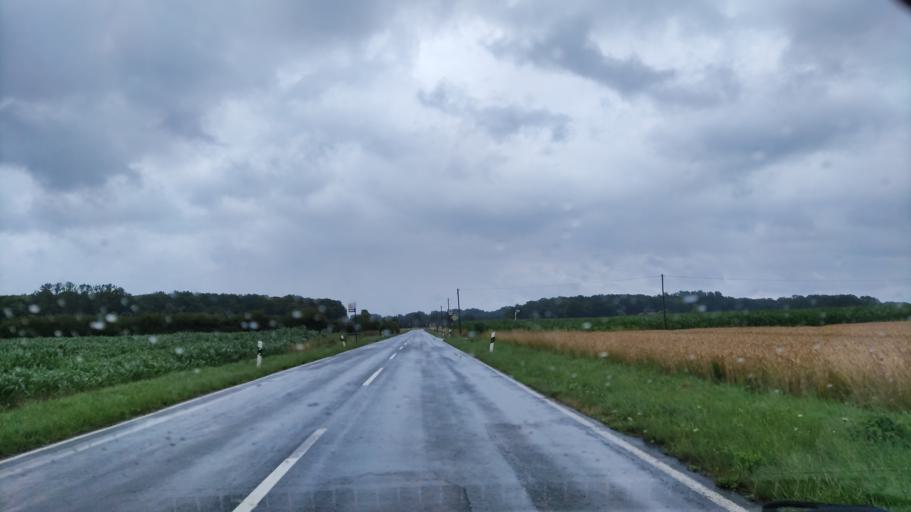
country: DE
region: North Rhine-Westphalia
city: Sendenhorst
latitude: 51.8907
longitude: 7.7813
